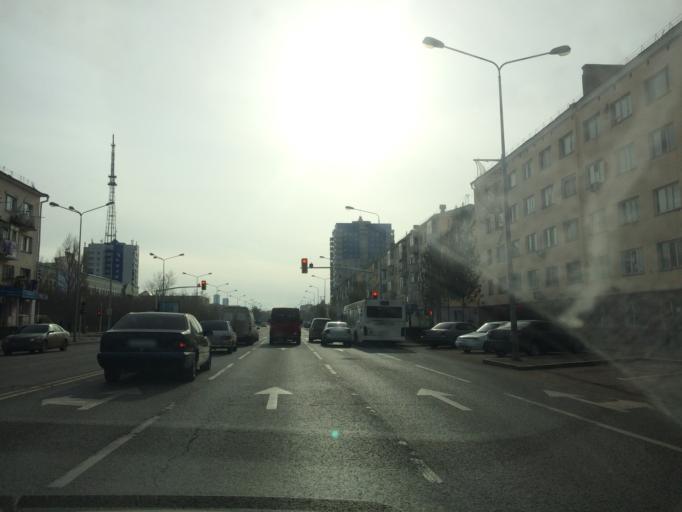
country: KZ
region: Astana Qalasy
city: Astana
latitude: 51.1886
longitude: 71.4074
